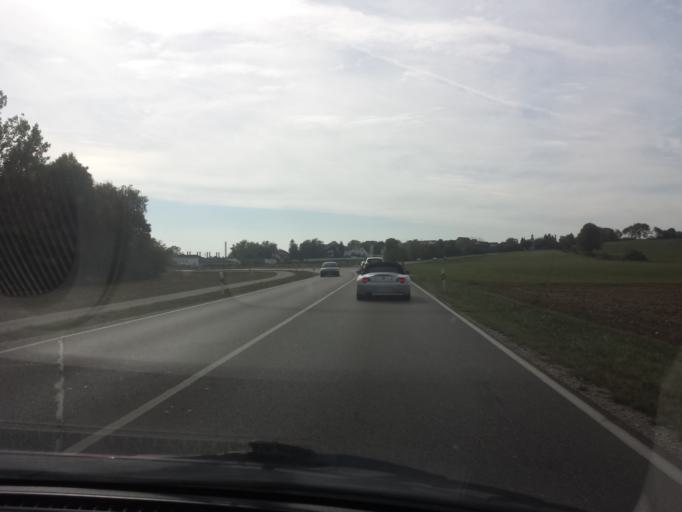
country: DE
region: Bavaria
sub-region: Upper Bavaria
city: Bergheim
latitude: 48.7628
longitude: 11.2720
